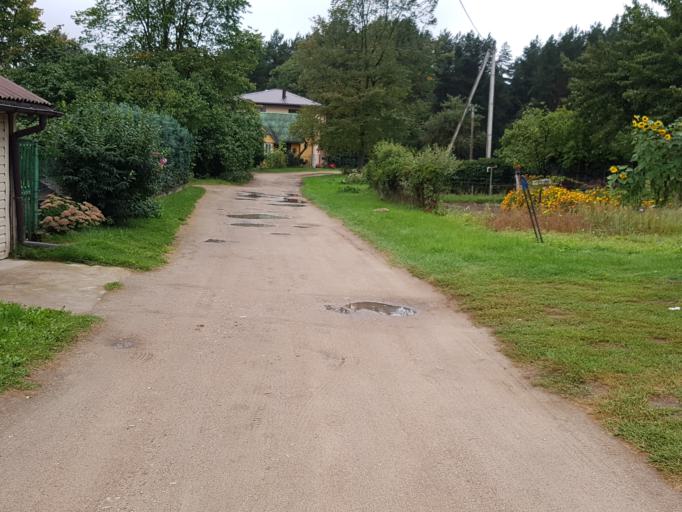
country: LT
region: Vilnius County
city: Lazdynai
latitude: 54.6507
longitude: 25.2071
